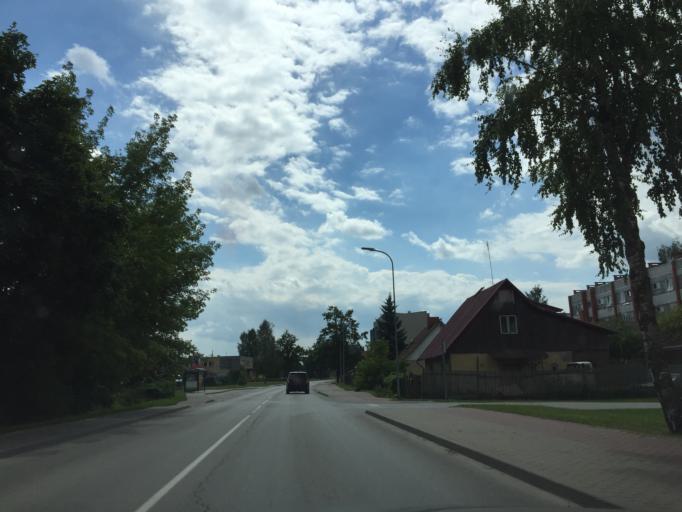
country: LV
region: Jelgava
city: Jelgava
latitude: 56.6361
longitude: 23.7082
